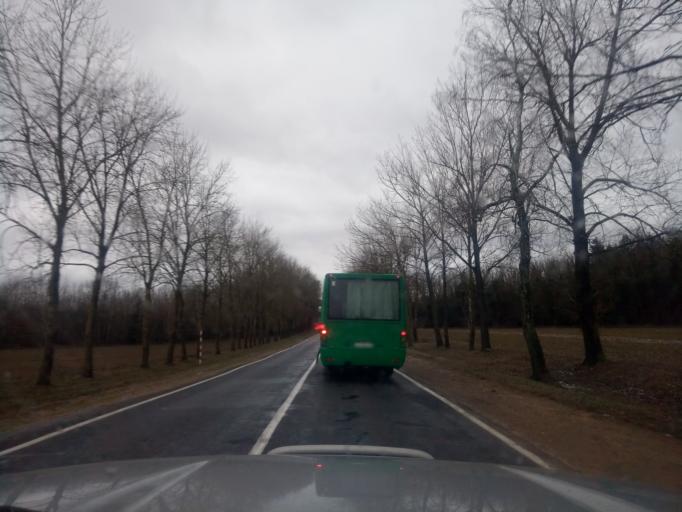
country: BY
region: Minsk
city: Kapyl'
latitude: 53.1711
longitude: 27.1452
